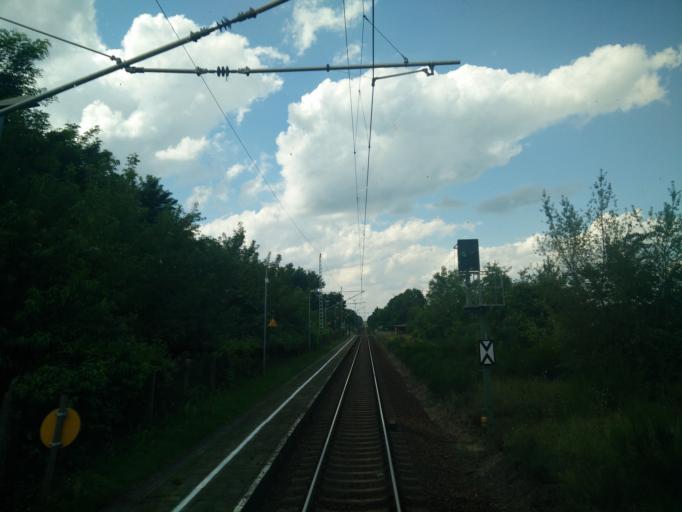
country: DE
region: Brandenburg
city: Vetschau
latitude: 51.8147
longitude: 14.0338
